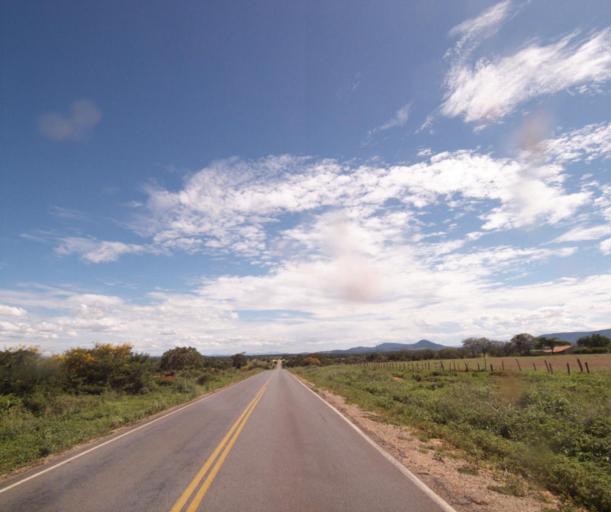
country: BR
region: Bahia
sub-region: Guanambi
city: Guanambi
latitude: -14.5417
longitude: -42.6991
